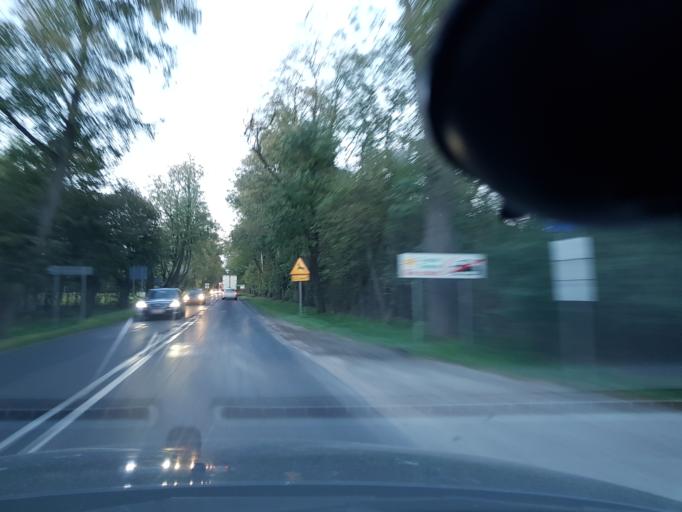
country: PL
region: Masovian Voivodeship
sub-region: Powiat grodziski
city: Grodzisk Mazowiecki
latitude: 52.0547
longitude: 20.6055
